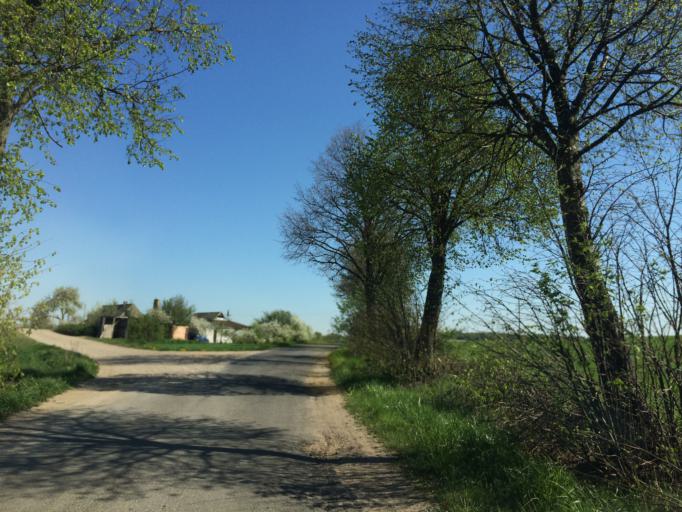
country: PL
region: Warmian-Masurian Voivodeship
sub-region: Powiat dzialdowski
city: Rybno
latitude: 53.4494
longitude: 19.9265
